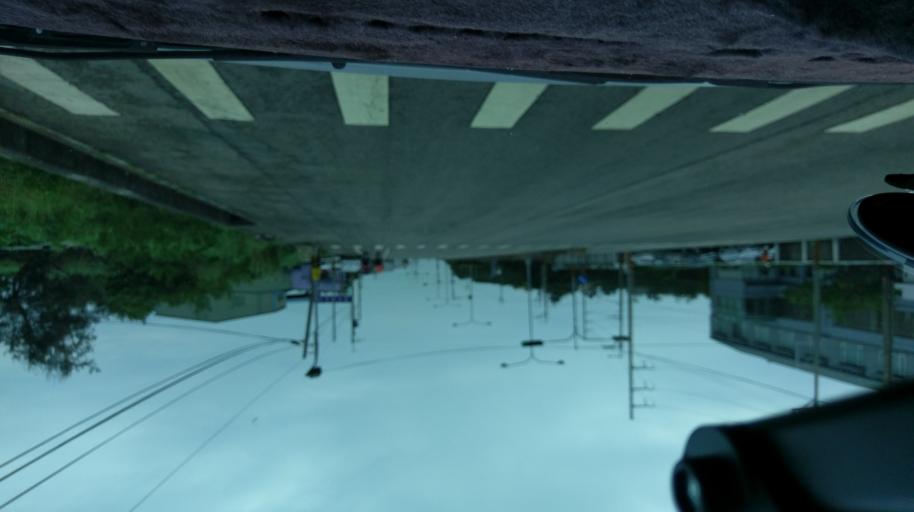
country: TW
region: Taiwan
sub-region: Miaoli
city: Miaoli
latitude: 24.4730
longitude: 120.6701
